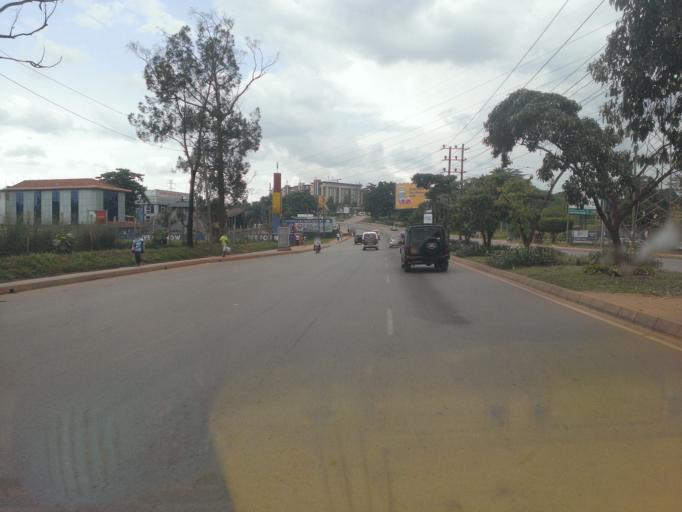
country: UG
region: Central Region
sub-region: Kampala District
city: Kampala
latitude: 0.3261
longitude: 32.6082
